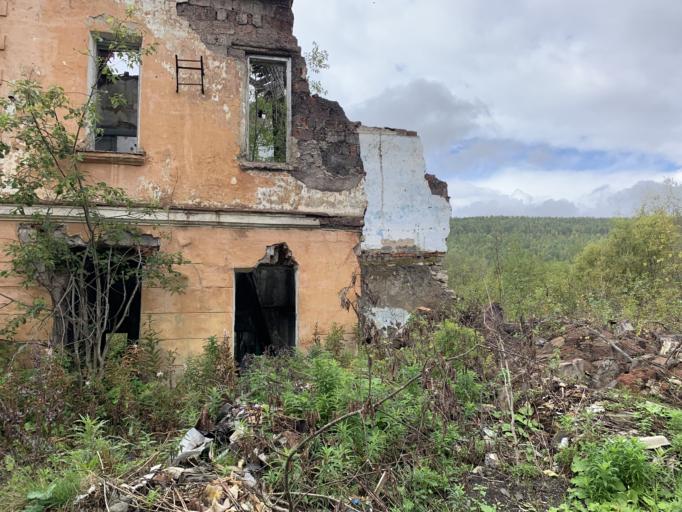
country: RU
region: Perm
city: Gubakha
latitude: 58.8733
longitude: 57.6017
